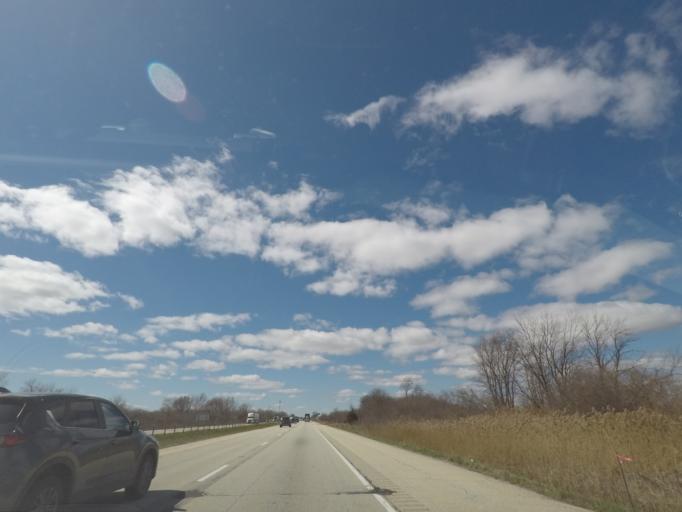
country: US
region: Illinois
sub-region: Grundy County
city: Central City
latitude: 41.2389
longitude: -88.2607
